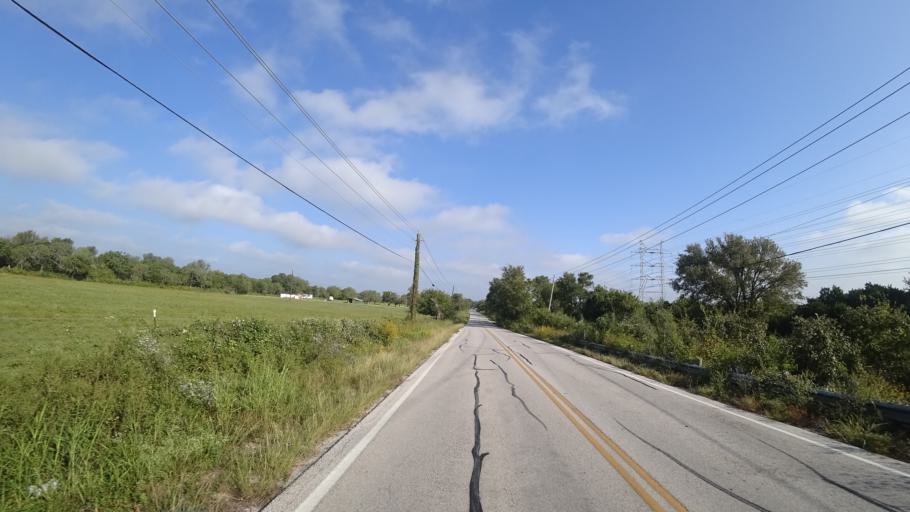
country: US
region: Texas
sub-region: Travis County
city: Manor
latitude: 30.3467
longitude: -97.6463
